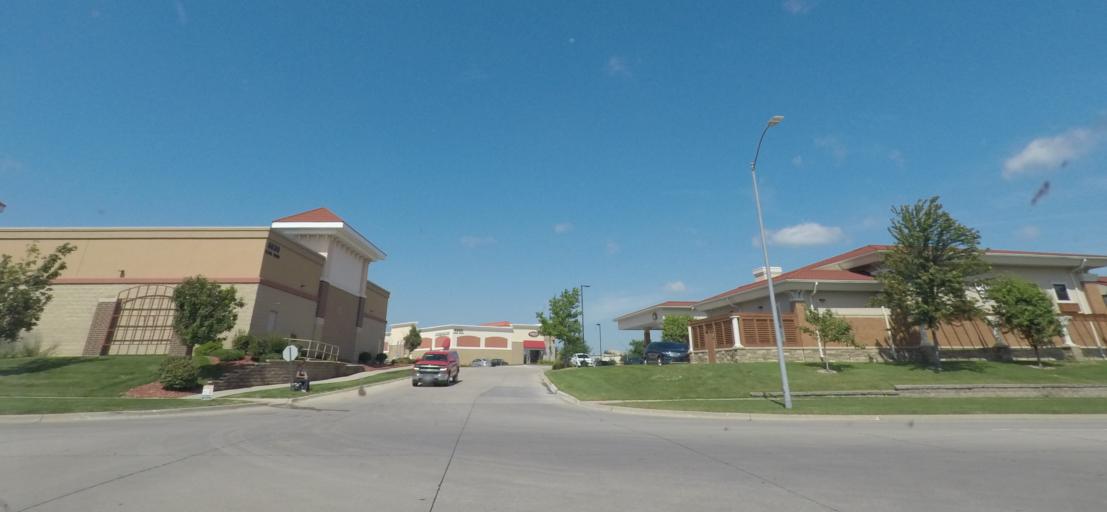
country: US
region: Iowa
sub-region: Polk County
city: Clive
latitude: 41.5606
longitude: -93.7975
